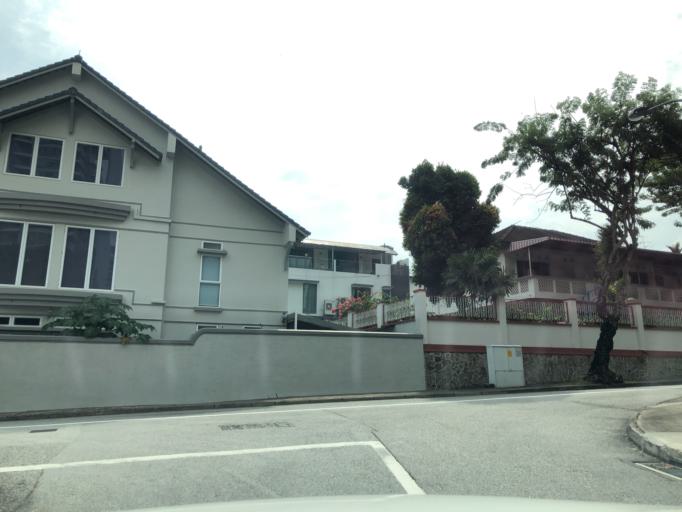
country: SG
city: Singapore
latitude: 1.3024
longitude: 103.8289
